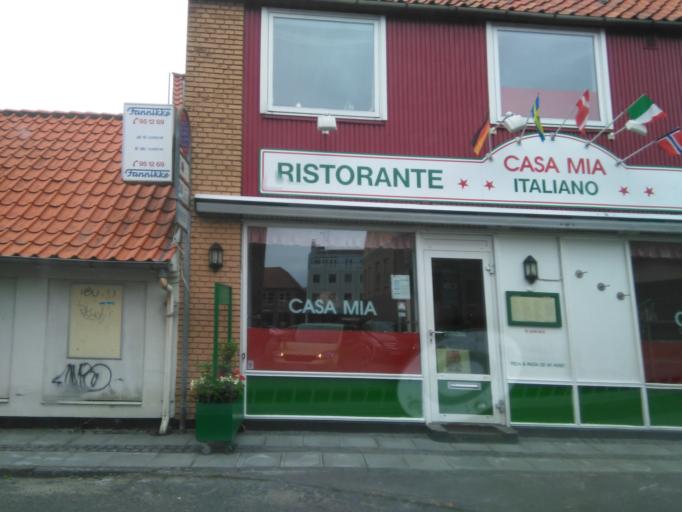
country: DK
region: Capital Region
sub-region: Bornholm Kommune
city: Ronne
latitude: 55.1018
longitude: 14.6982
